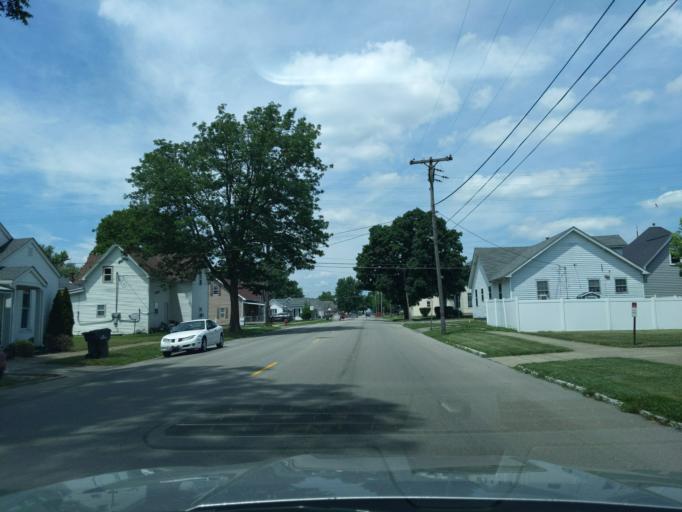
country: US
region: Indiana
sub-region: Decatur County
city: Greensburg
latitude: 39.3382
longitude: -85.4890
